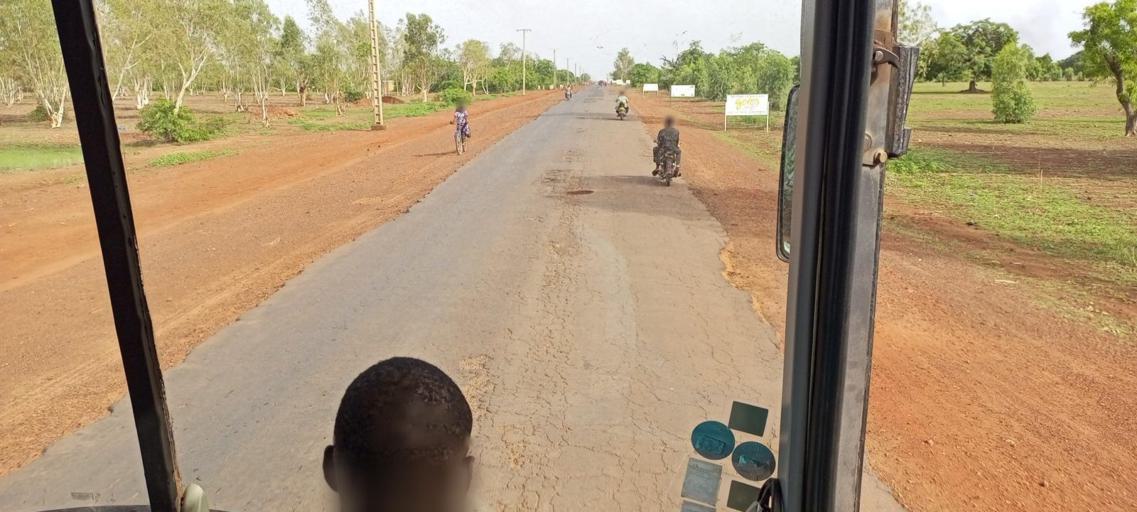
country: ML
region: Sikasso
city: Koutiala
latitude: 12.4340
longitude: -5.4793
